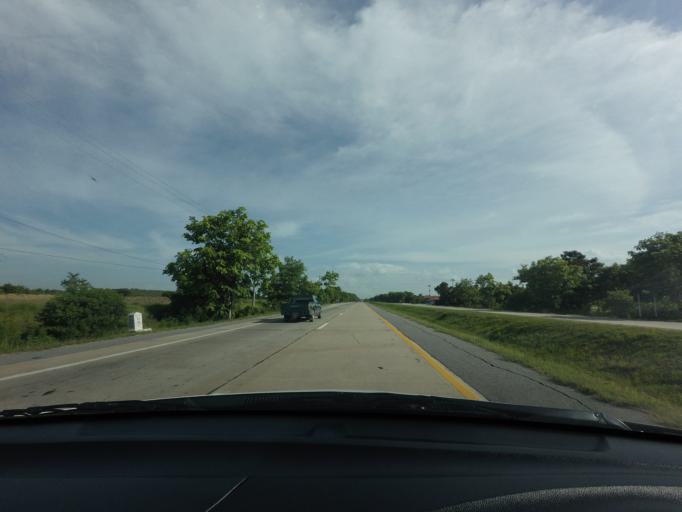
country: TH
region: Suphan Buri
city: Suphan Buri
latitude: 14.4909
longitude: 100.0451
